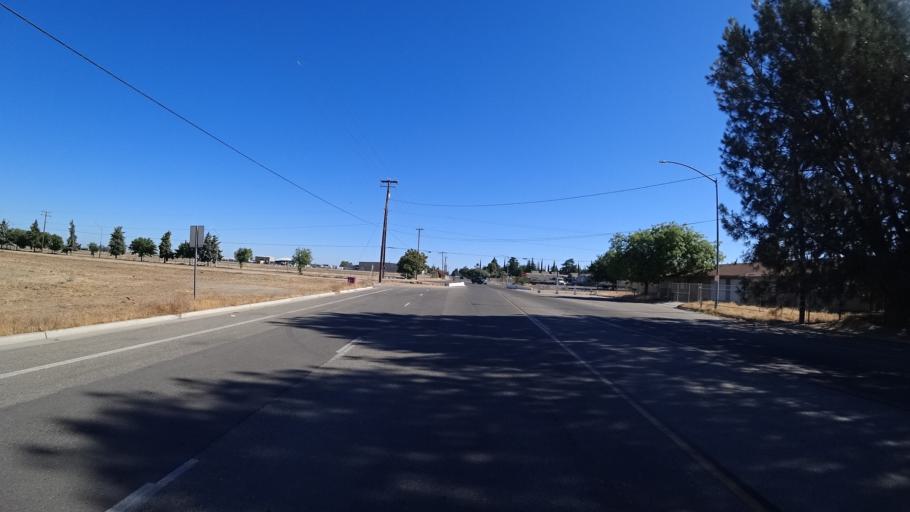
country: US
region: California
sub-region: Fresno County
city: West Park
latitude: 36.7424
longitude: -119.8357
